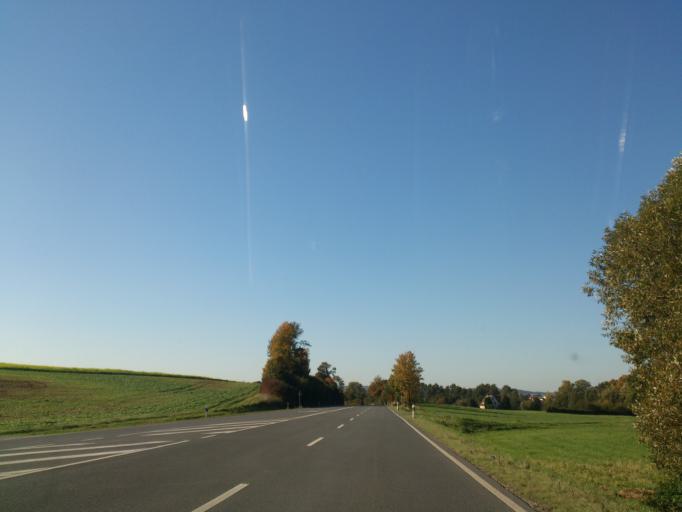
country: DE
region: Hesse
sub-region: Regierungsbezirk Kassel
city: Calden
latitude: 51.4287
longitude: 9.3409
